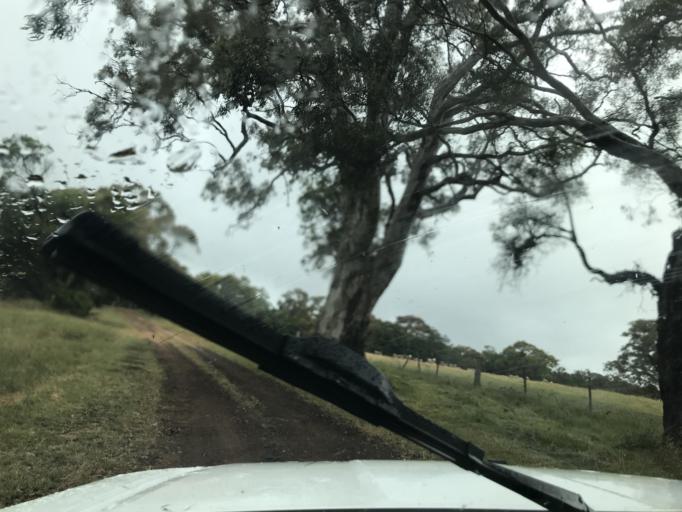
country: AU
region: South Australia
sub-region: Wattle Range
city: Penola
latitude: -37.2532
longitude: 141.3349
